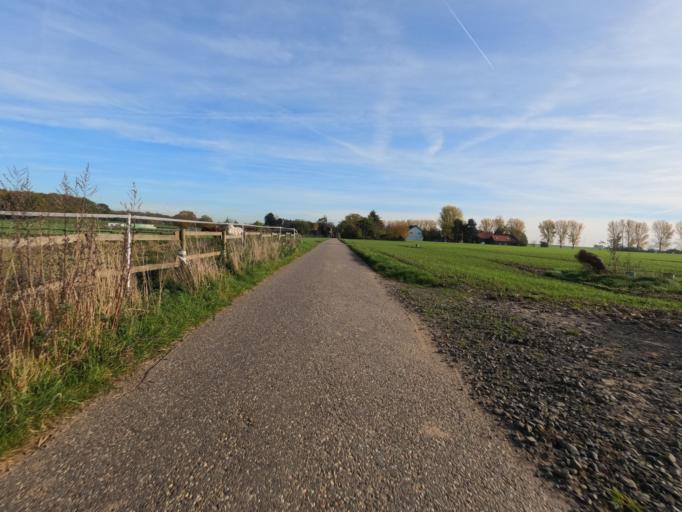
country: DE
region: North Rhine-Westphalia
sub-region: Regierungsbezirk Koln
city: Titz
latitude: 51.0786
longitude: 6.3978
